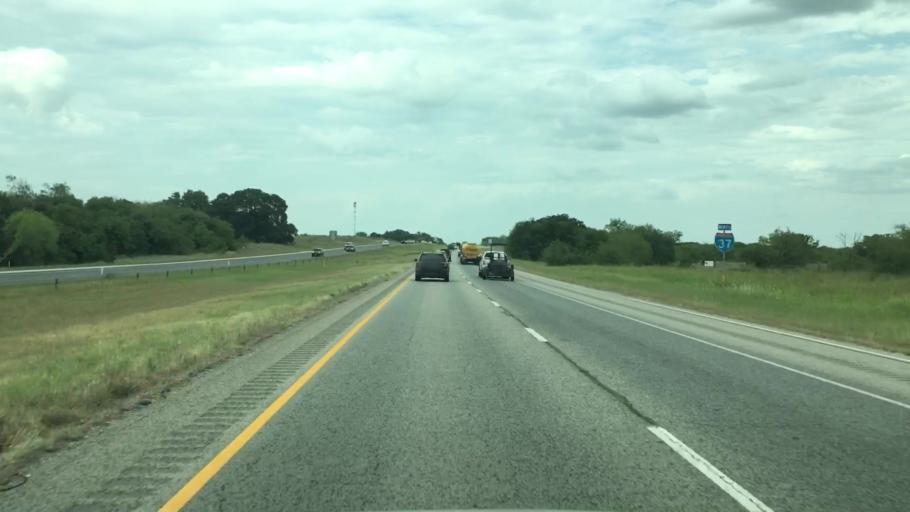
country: US
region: Texas
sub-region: Atascosa County
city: Pleasanton
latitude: 29.1145
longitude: -98.4319
